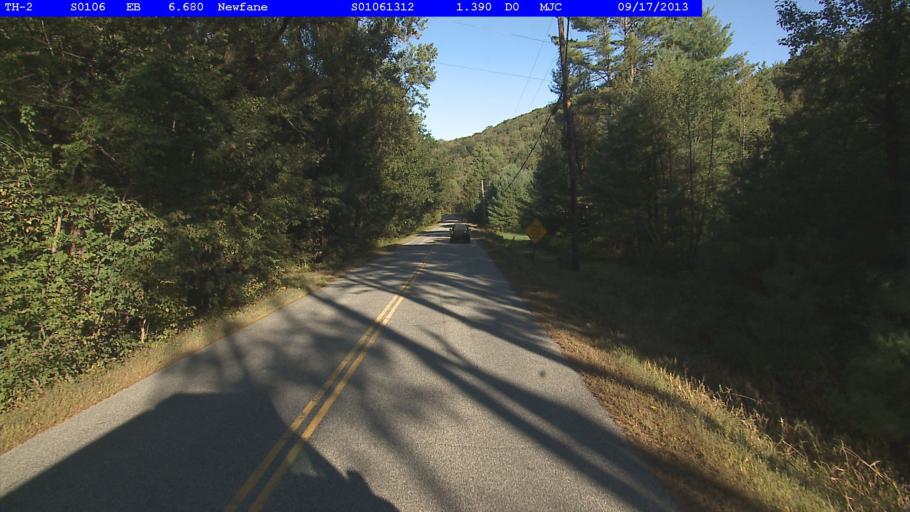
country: US
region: Vermont
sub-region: Windham County
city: Dover
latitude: 42.9446
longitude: -72.7425
